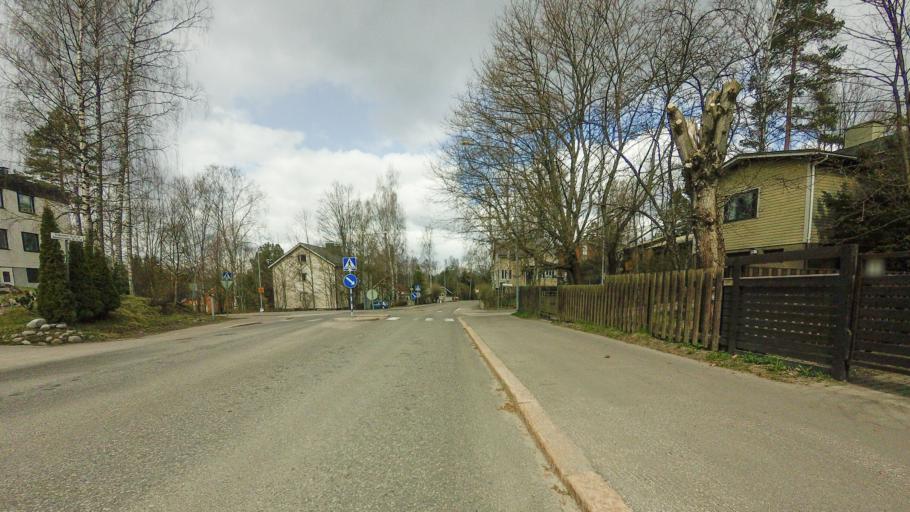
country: FI
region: Uusimaa
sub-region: Helsinki
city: Vantaa
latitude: 60.2209
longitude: 25.0952
